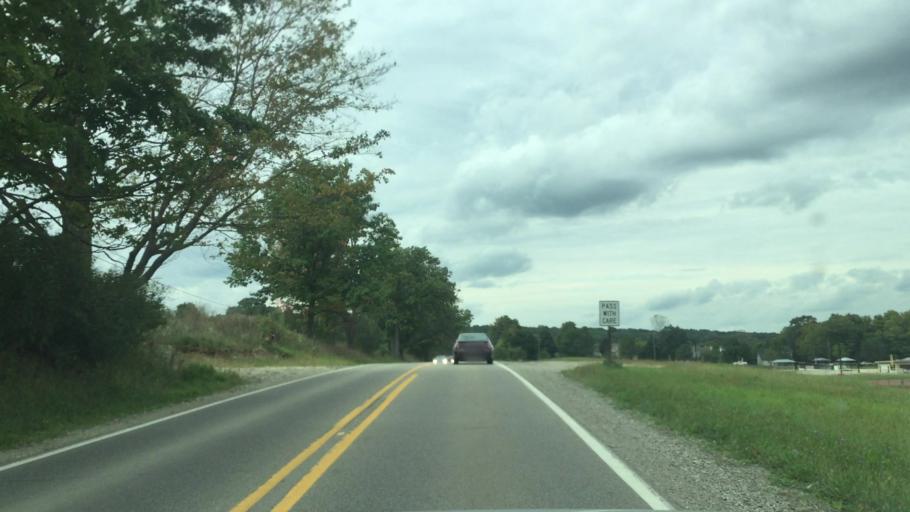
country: US
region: Michigan
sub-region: Livingston County
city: Whitmore Lake
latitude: 42.4643
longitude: -83.7611
